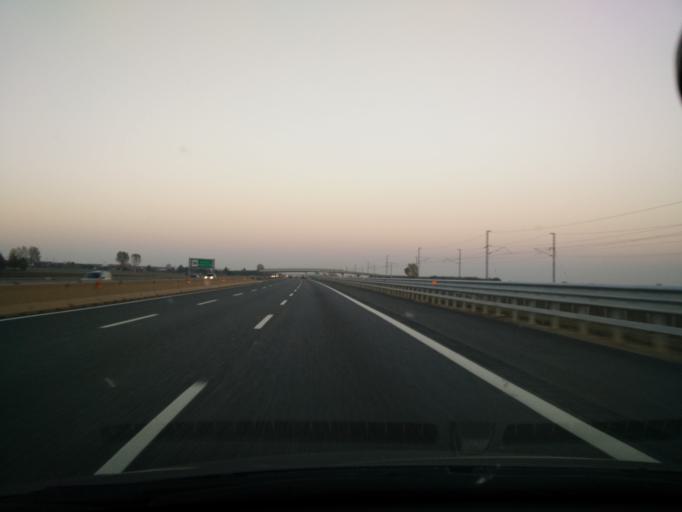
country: IT
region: Piedmont
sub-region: Provincia di Vercelli
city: Saluggia
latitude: 45.2586
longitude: 8.0048
